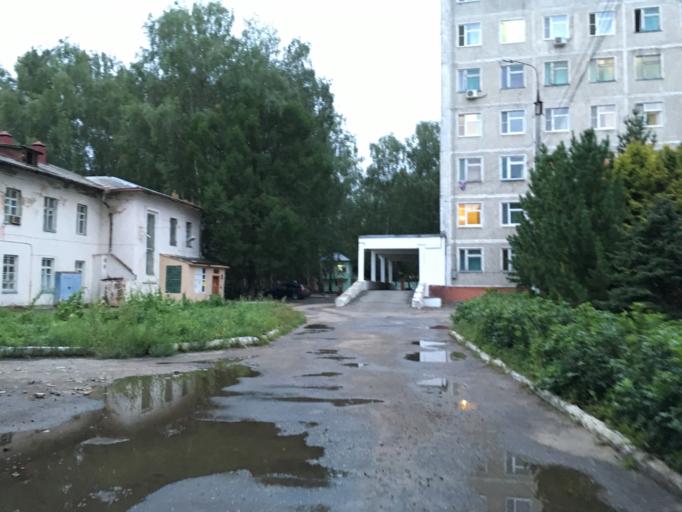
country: RU
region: Mariy-El
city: Yoshkar-Ola
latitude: 56.6494
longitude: 47.8851
